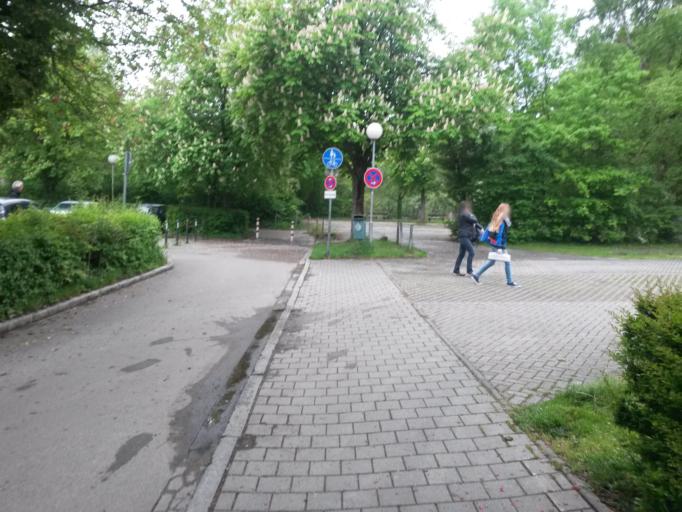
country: DE
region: Bavaria
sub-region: Upper Bavaria
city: Ingolstadt
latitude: 48.7617
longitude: 11.4186
